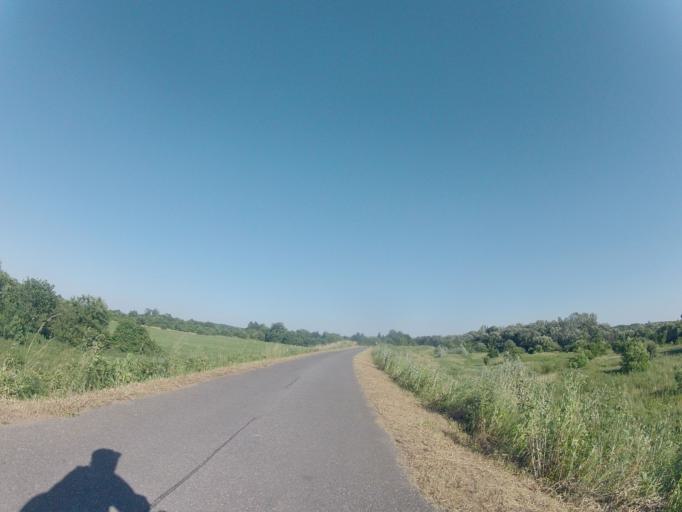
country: PL
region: Lesser Poland Voivodeship
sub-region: Krakow
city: Sidzina
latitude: 50.0448
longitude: 19.8742
